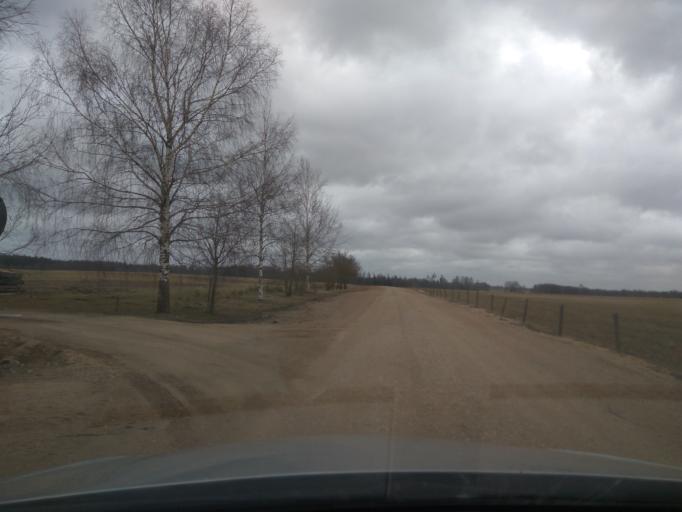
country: LV
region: Skrunda
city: Skrunda
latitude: 56.8460
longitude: 22.2292
